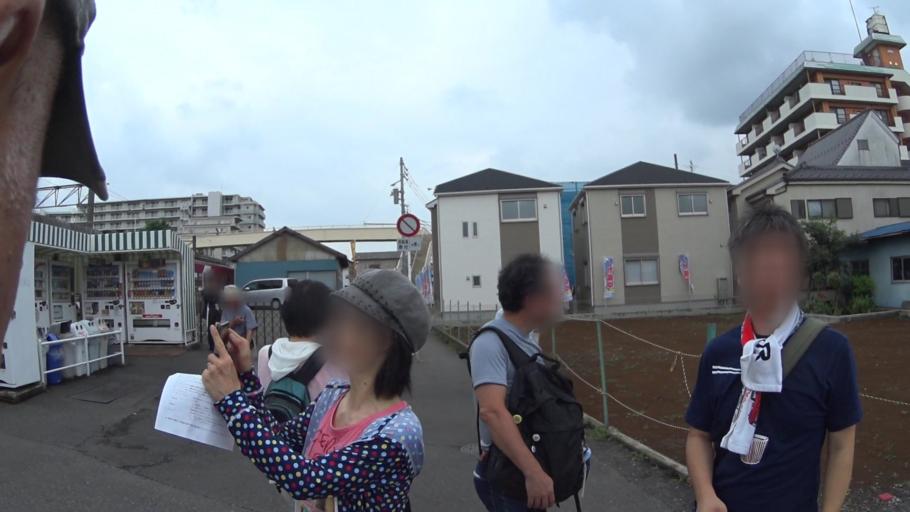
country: JP
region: Chiba
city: Nagareyama
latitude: 35.8558
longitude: 139.9015
